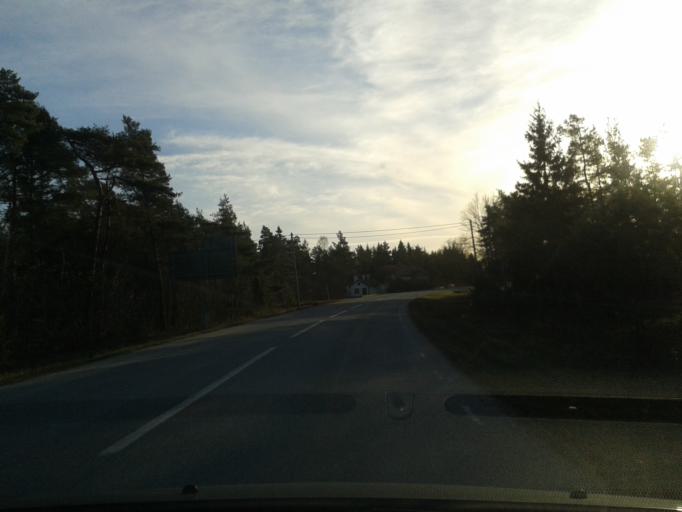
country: SE
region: Gotland
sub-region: Gotland
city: Hemse
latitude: 57.3610
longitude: 18.6849
